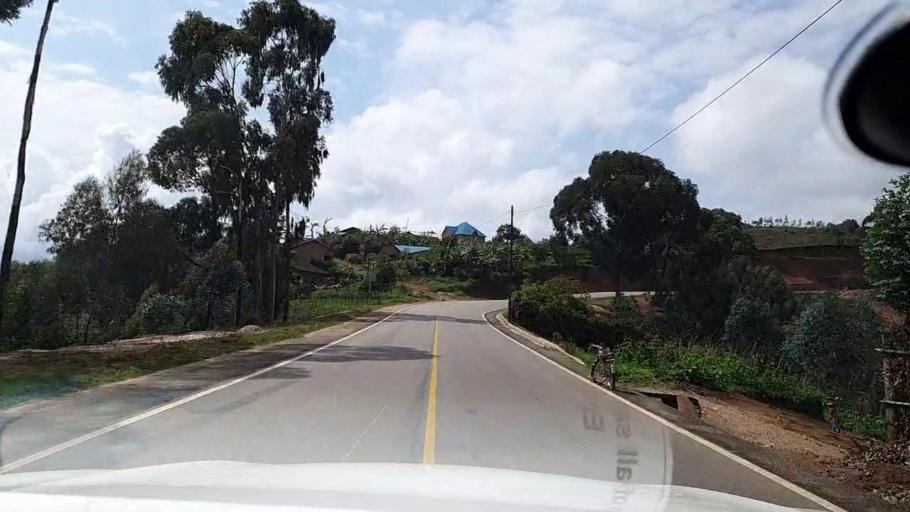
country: RW
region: Southern Province
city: Nzega
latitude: -2.4901
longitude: 29.5115
